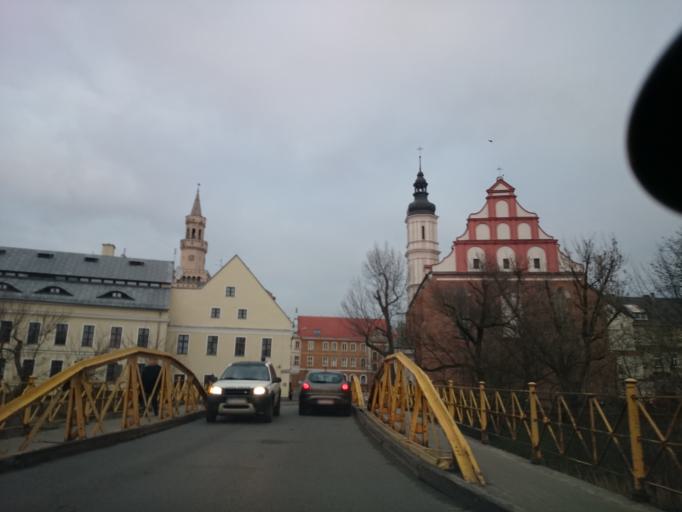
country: PL
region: Opole Voivodeship
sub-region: Powiat opolski
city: Opole
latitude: 50.6675
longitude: 17.9207
